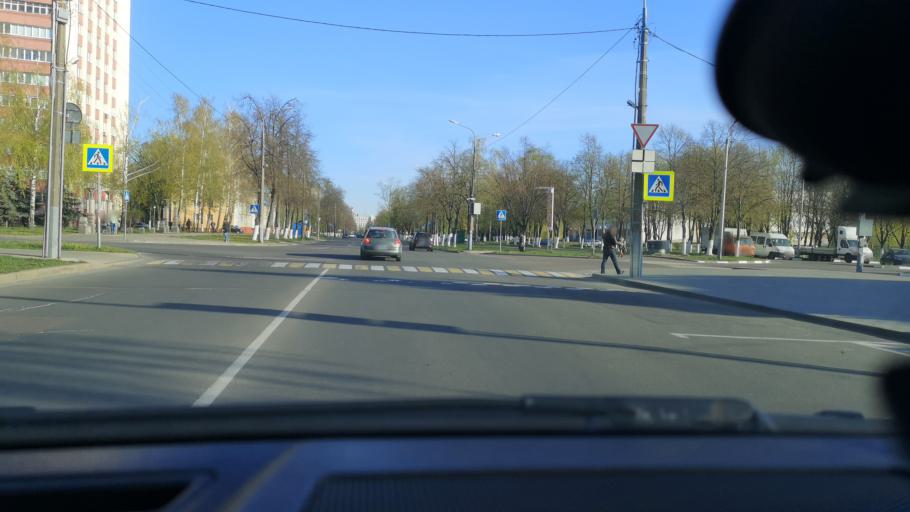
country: BY
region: Gomel
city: Gomel
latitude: 52.4525
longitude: 31.0062
